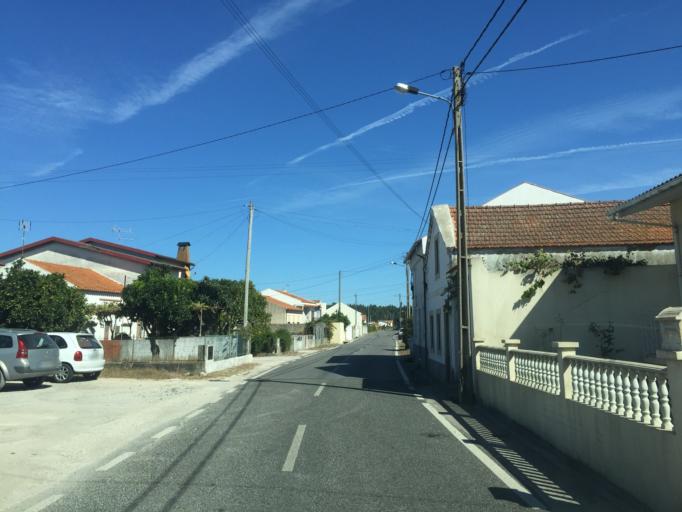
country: PT
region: Coimbra
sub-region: Figueira da Foz
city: Tavarede
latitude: 40.2151
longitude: -8.8457
